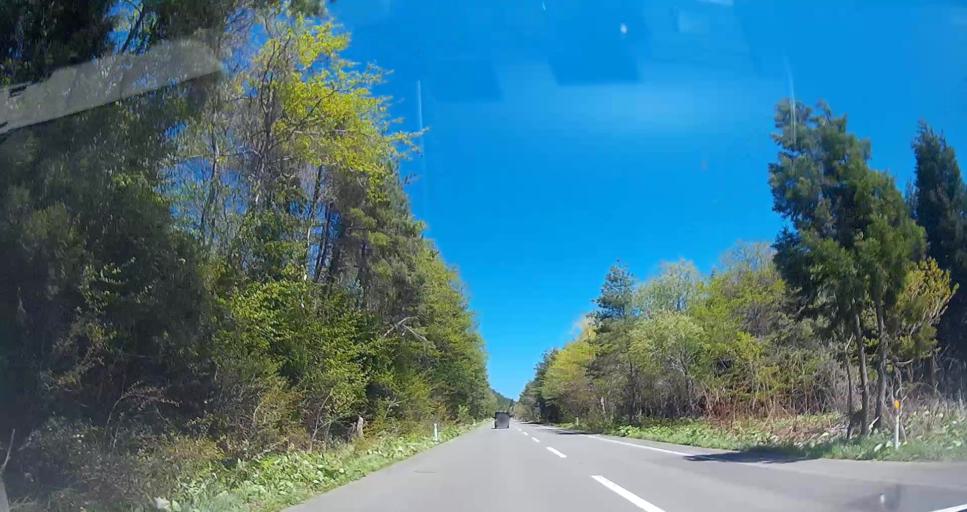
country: JP
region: Aomori
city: Mutsu
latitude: 41.3148
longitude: 141.4001
